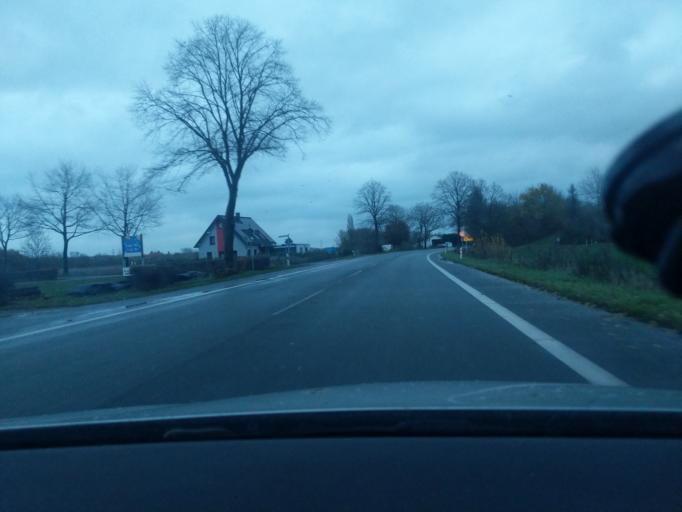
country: DE
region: North Rhine-Westphalia
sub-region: Regierungsbezirk Arnsberg
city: Hamm
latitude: 51.6975
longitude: 7.8783
